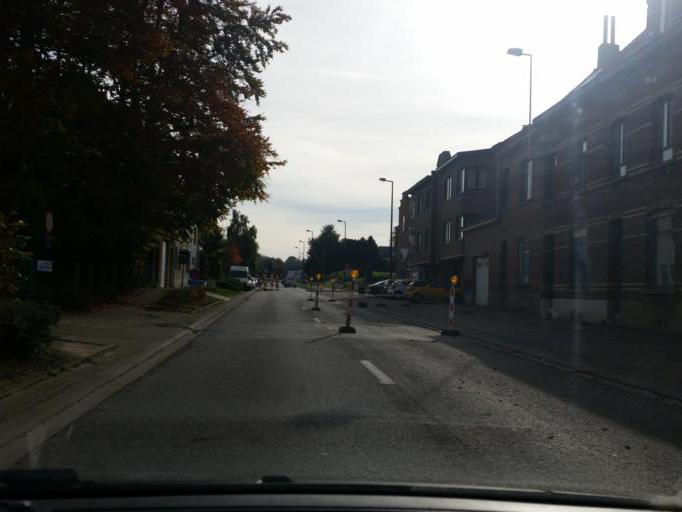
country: BE
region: Flanders
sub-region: Provincie Vlaams-Brabant
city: Grimbergen
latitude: 50.9314
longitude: 4.3653
